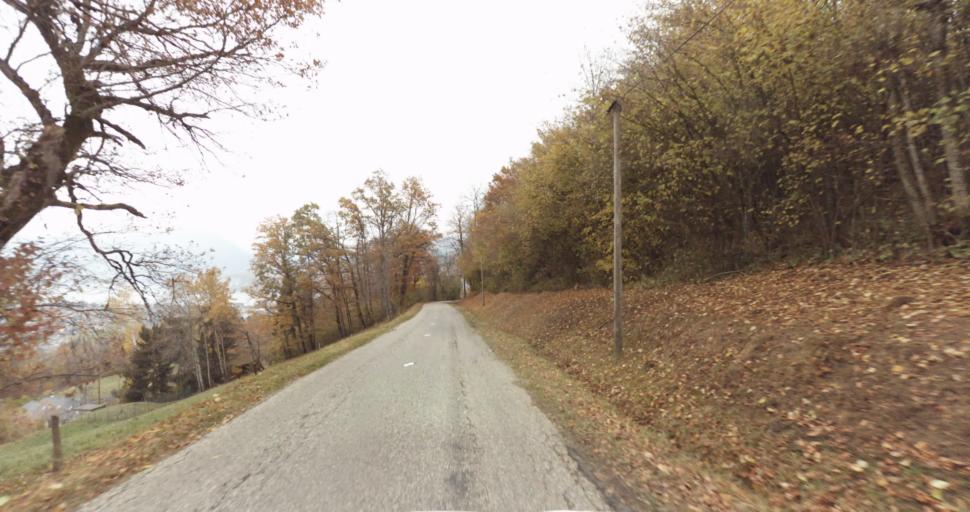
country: FR
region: Rhone-Alpes
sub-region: Departement de la Haute-Savoie
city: Saint-Jorioz
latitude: 45.8144
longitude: 6.1685
